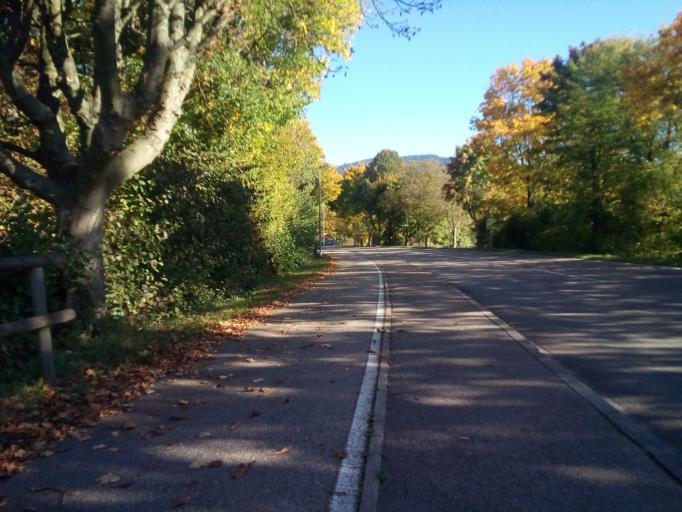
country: DE
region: Baden-Wuerttemberg
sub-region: Karlsruhe Region
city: Buhl
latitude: 48.6866
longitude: 8.1369
